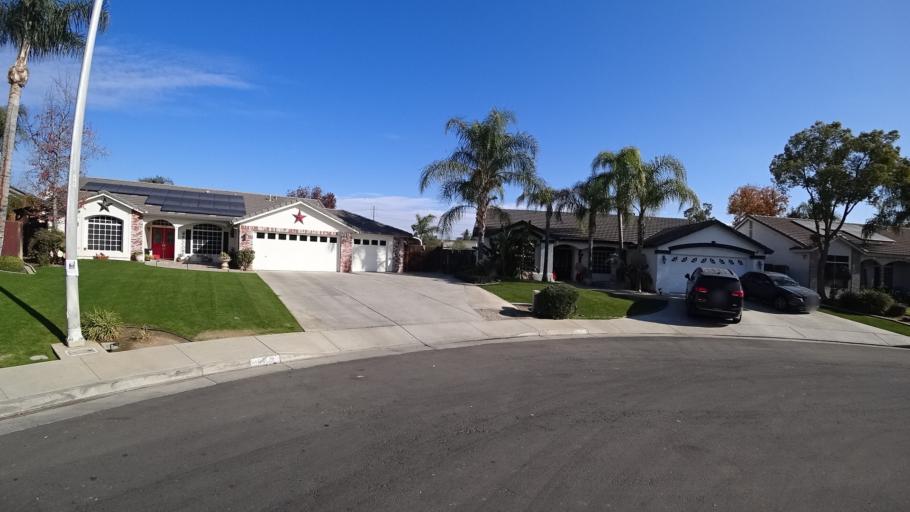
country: US
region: California
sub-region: Kern County
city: Greenacres
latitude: 35.4028
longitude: -119.0946
